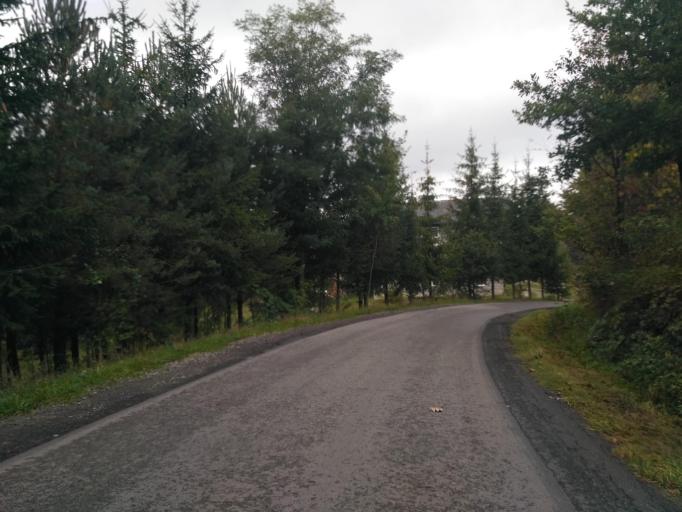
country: PL
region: Subcarpathian Voivodeship
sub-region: Powiat debicki
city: Brzostek
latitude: 49.9253
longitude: 21.4638
